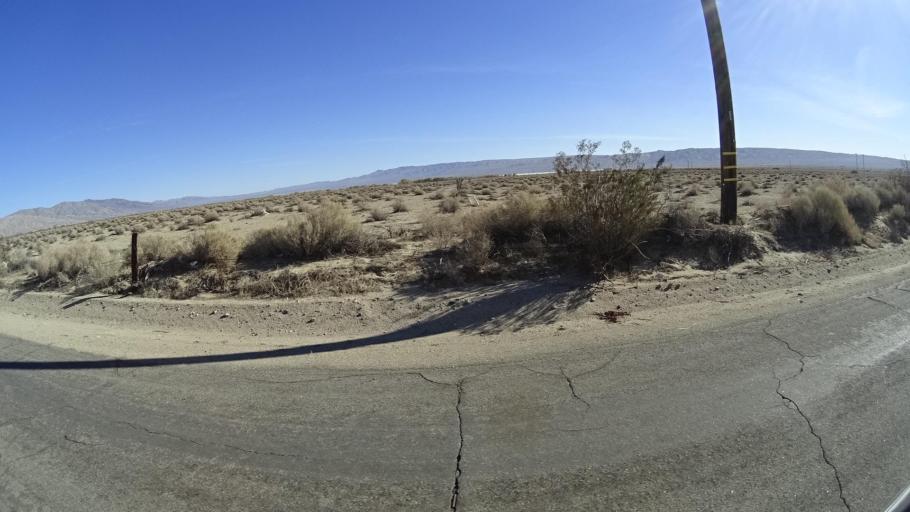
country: US
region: California
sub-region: Kern County
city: California City
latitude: 35.3109
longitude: -117.9504
